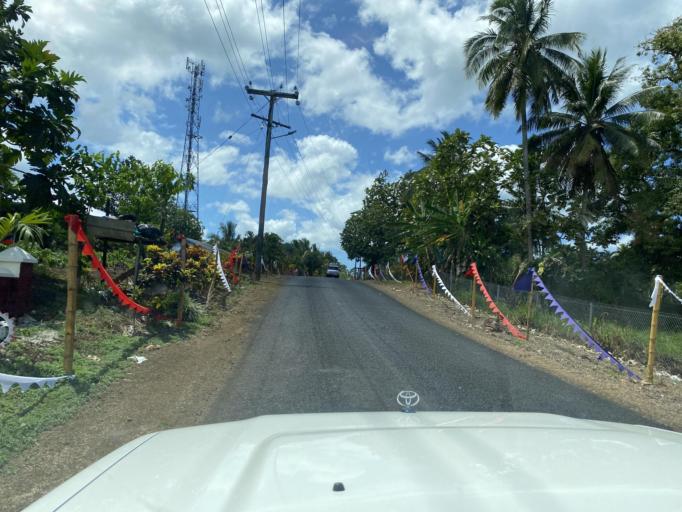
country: WS
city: Lotofaga
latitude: -14.0049
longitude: -171.7888
